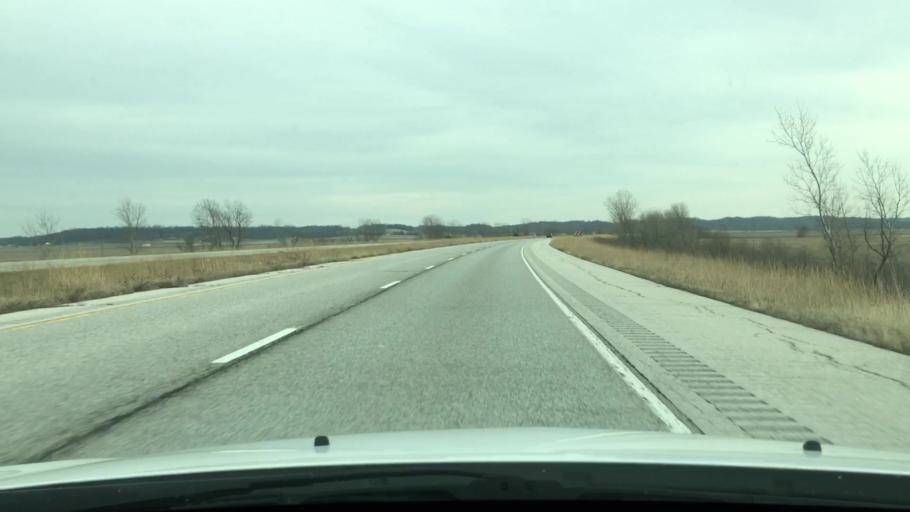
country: US
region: Illinois
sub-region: Pike County
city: Griggsville
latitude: 39.6914
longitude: -90.6089
